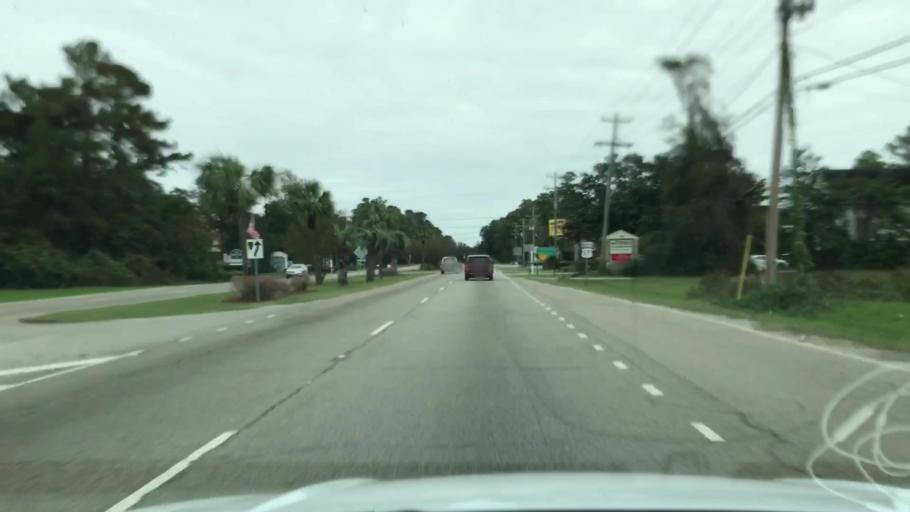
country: US
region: South Carolina
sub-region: Georgetown County
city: Murrells Inlet
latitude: 33.4726
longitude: -79.1042
